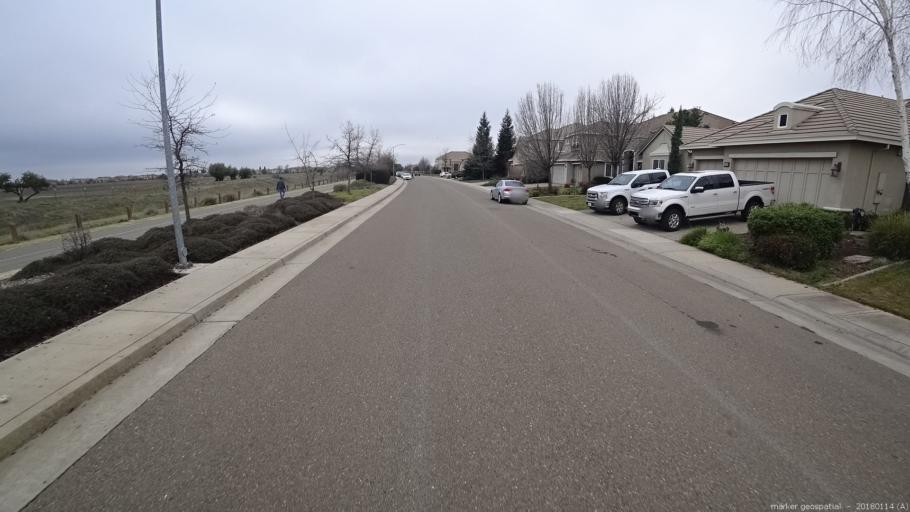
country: US
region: California
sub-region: Sacramento County
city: Gold River
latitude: 38.5429
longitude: -121.2298
